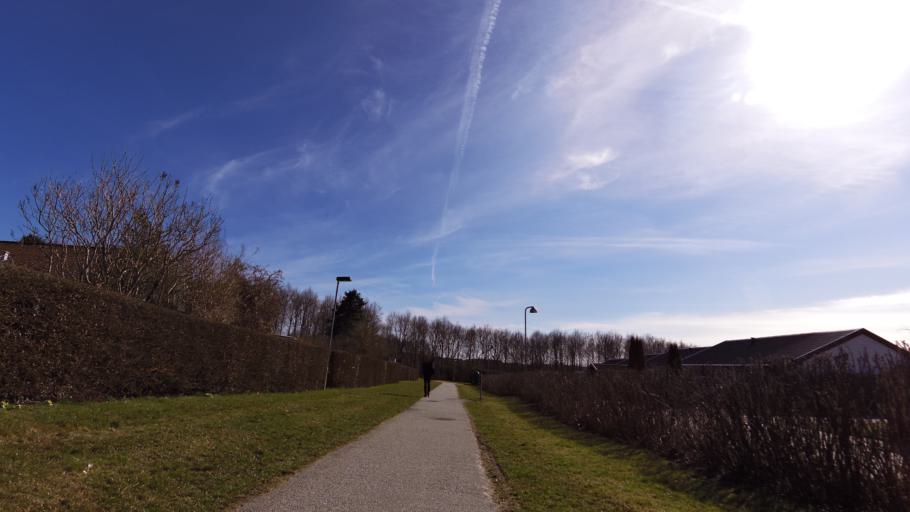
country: DK
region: Central Jutland
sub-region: Arhus Kommune
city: Stavtrup
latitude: 56.1745
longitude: 10.1040
